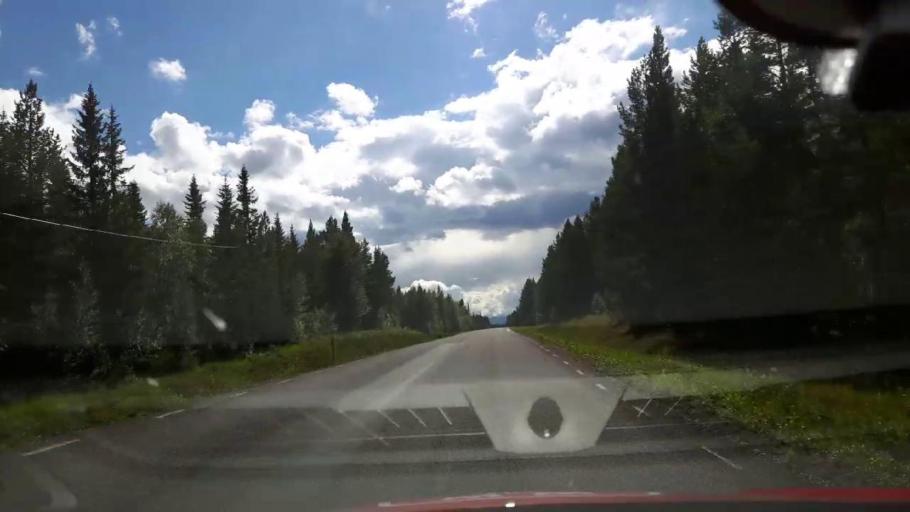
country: SE
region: Jaemtland
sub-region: Are Kommun
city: Are
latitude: 63.2043
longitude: 13.1605
